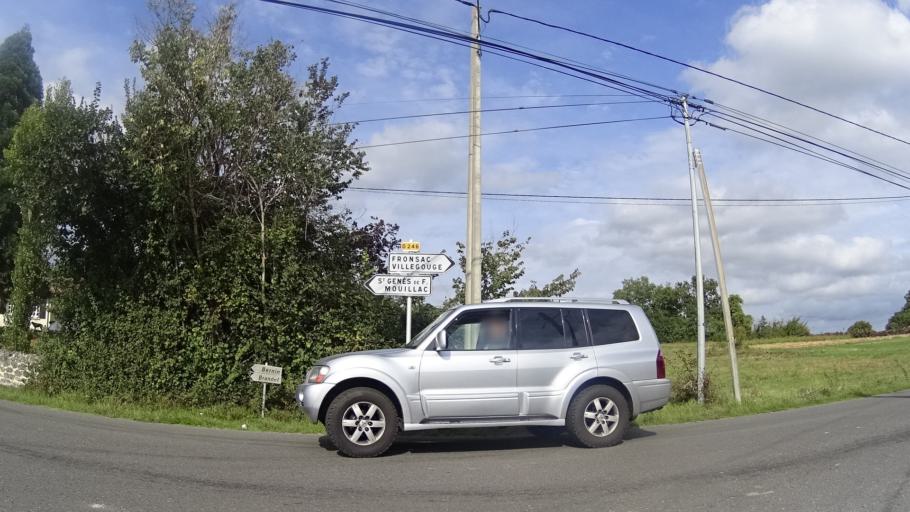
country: FR
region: Aquitaine
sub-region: Departement de la Gironde
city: Lugon-et-l'Ile-du-Carnay
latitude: 44.9922
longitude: -0.3430
